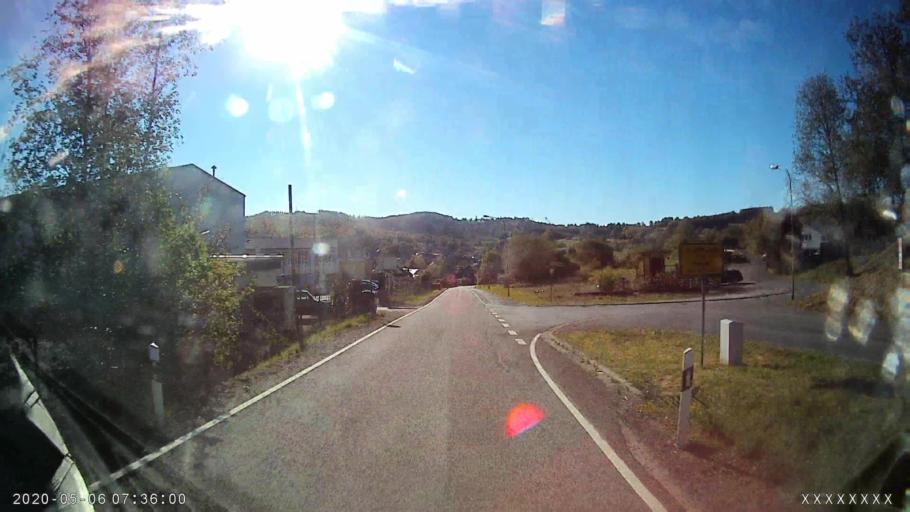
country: DE
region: Hesse
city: Dillenburg
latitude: 50.8154
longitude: 8.2637
